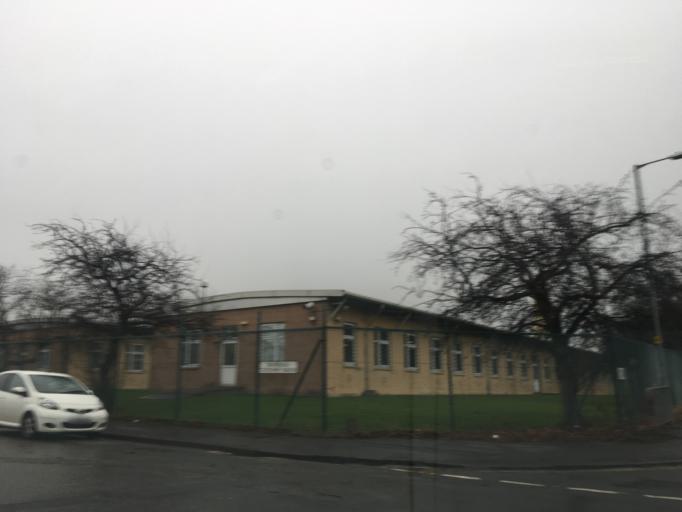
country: GB
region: Scotland
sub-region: Edinburgh
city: Currie
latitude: 55.9249
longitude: -3.2953
